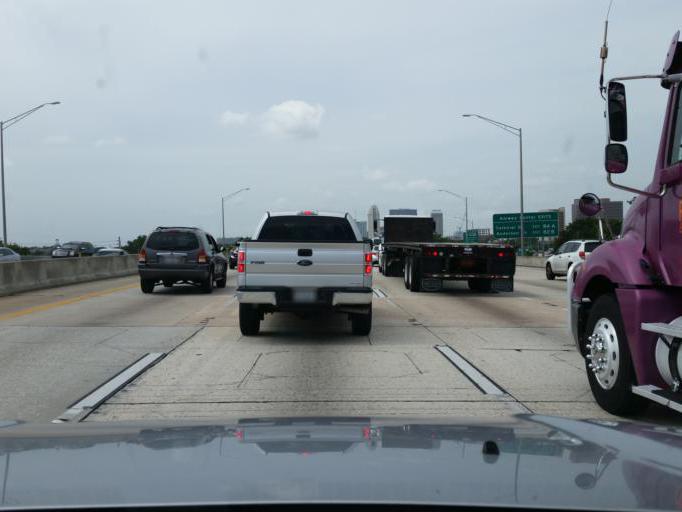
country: US
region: Florida
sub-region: Orange County
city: Fairview Shores
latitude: 28.5681
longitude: -81.3758
